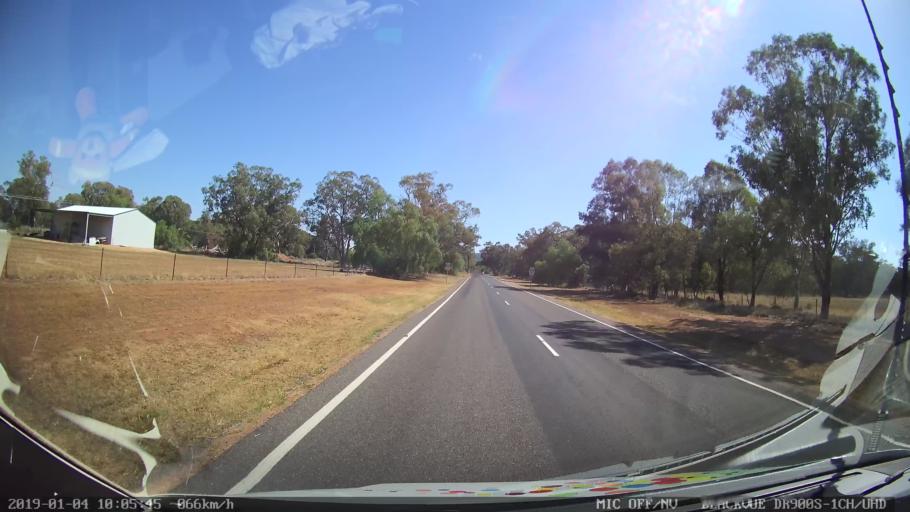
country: AU
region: New South Wales
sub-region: Cabonne
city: Canowindra
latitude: -33.4382
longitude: 148.3663
